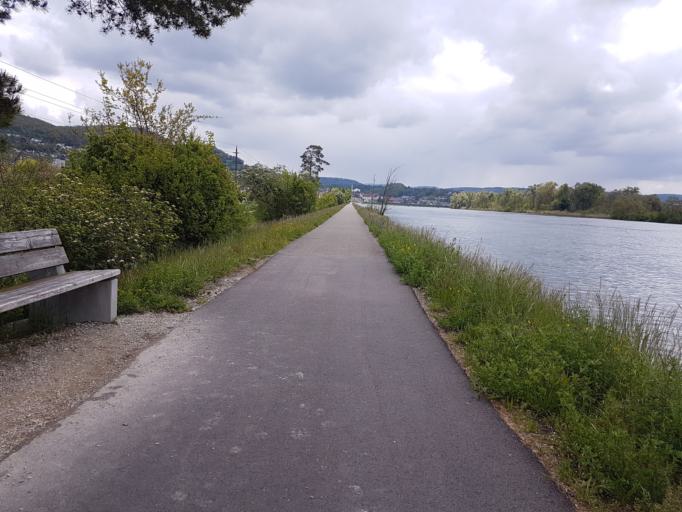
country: CH
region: Aargau
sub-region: Bezirk Zurzach
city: Klingnau
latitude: 47.5802
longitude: 8.2447
